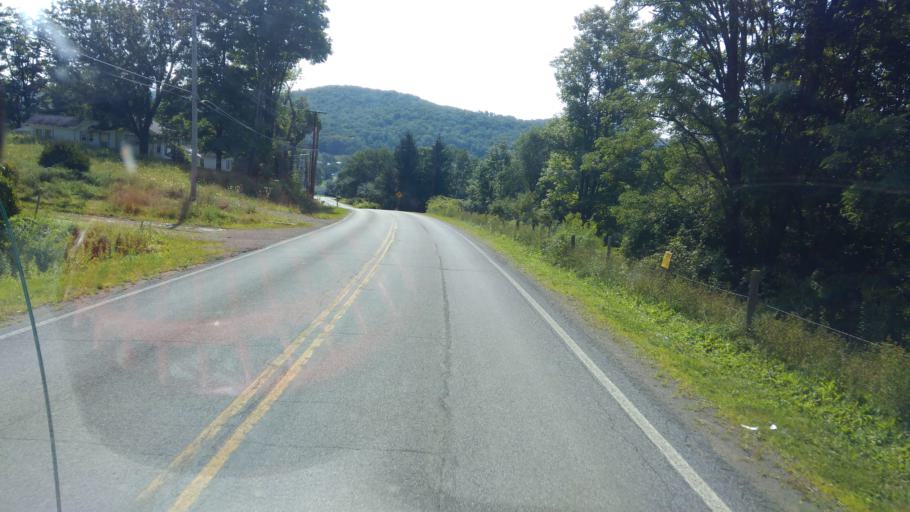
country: US
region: New York
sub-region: Allegany County
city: Bolivar
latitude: 42.0944
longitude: -78.1586
